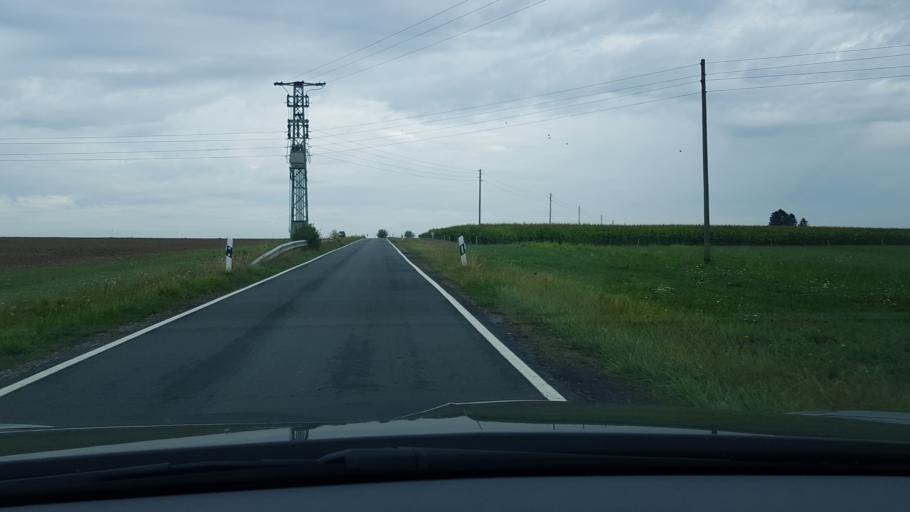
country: DE
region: Rheinland-Pfalz
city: Lof
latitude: 50.2364
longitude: 7.4253
